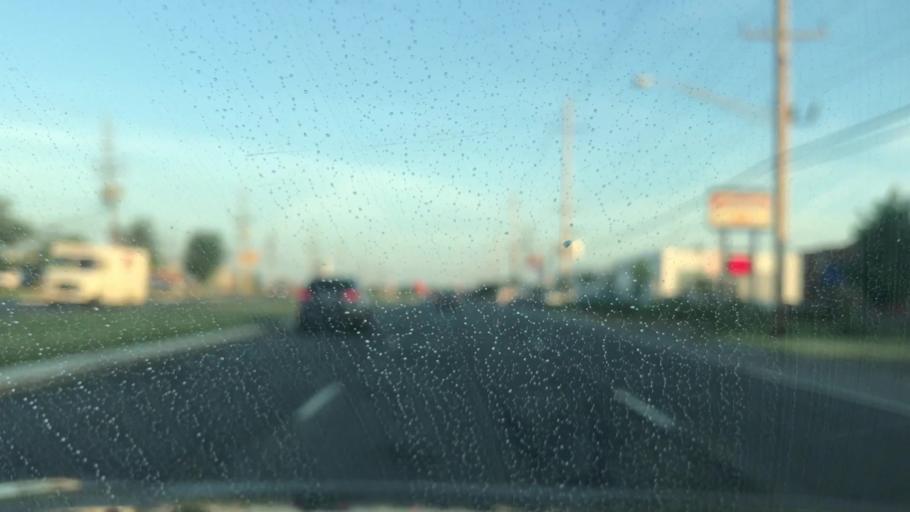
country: US
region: New Jersey
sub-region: Ocean County
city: Toms River
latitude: 39.9609
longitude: -74.1780
